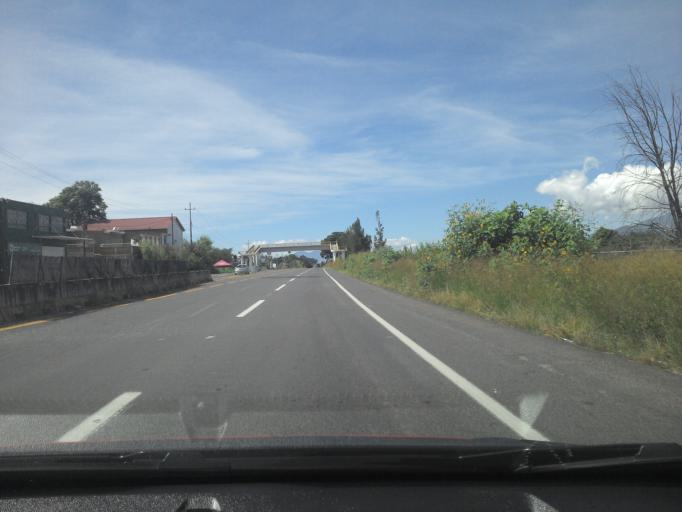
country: MX
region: Jalisco
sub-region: Tala
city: Los Ruisenores
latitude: 20.7207
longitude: -103.6252
